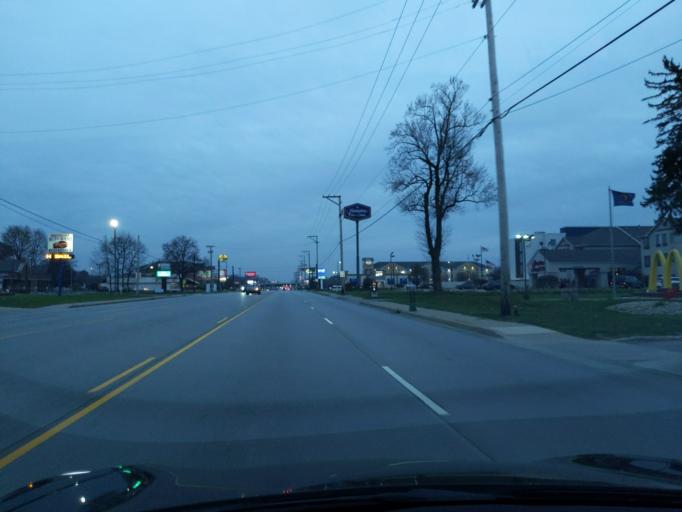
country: US
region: Indiana
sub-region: Saint Joseph County
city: Georgetown
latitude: 41.7277
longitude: -86.2506
